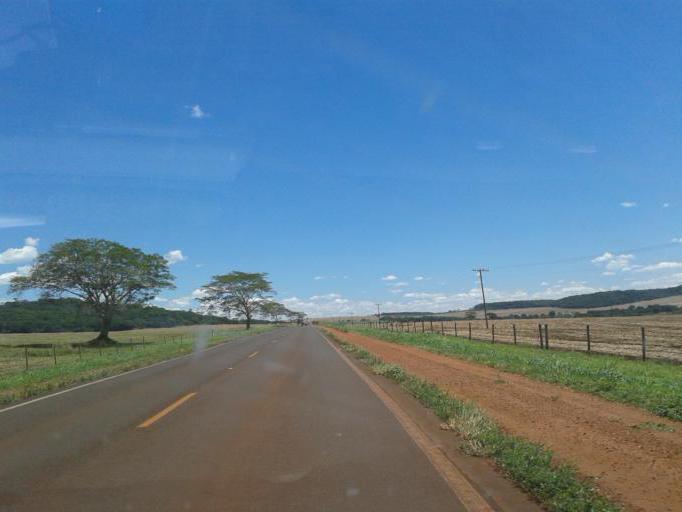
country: BR
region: Minas Gerais
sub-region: Capinopolis
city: Capinopolis
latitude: -18.6063
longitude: -49.5254
